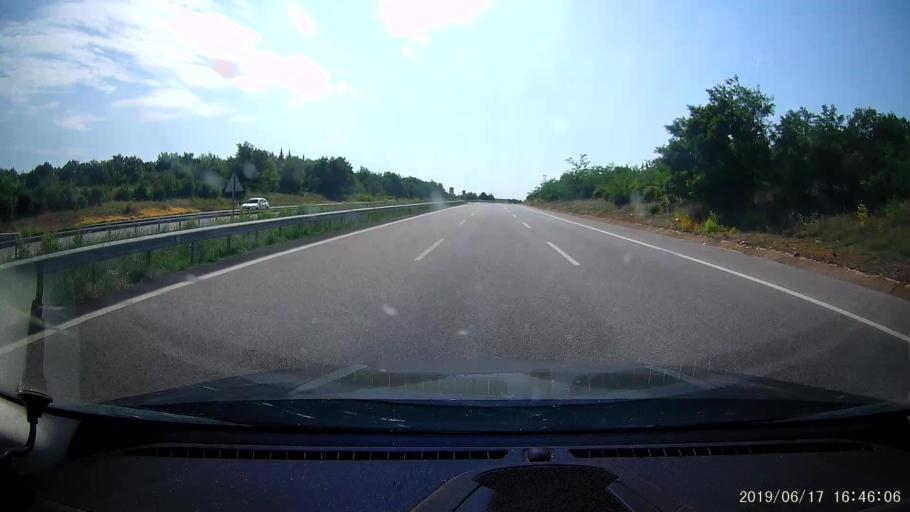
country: TR
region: Kirklareli
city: Babaeski
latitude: 41.4944
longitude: 27.2132
